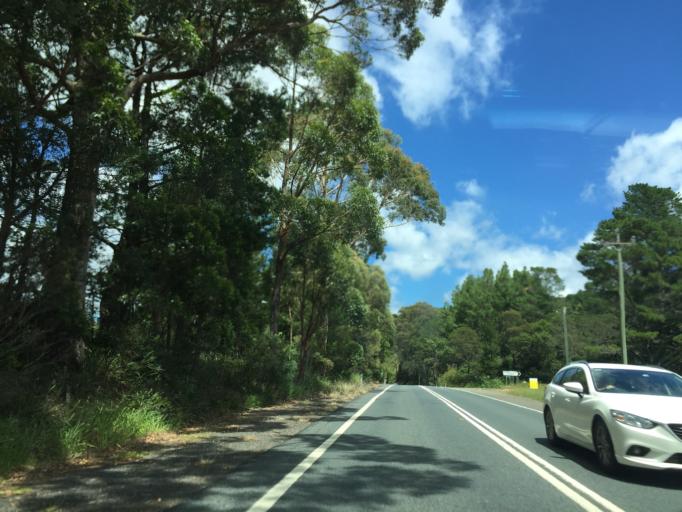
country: AU
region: New South Wales
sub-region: Blue Mountains Municipality
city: Hazelbrook
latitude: -33.5075
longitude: 150.4982
